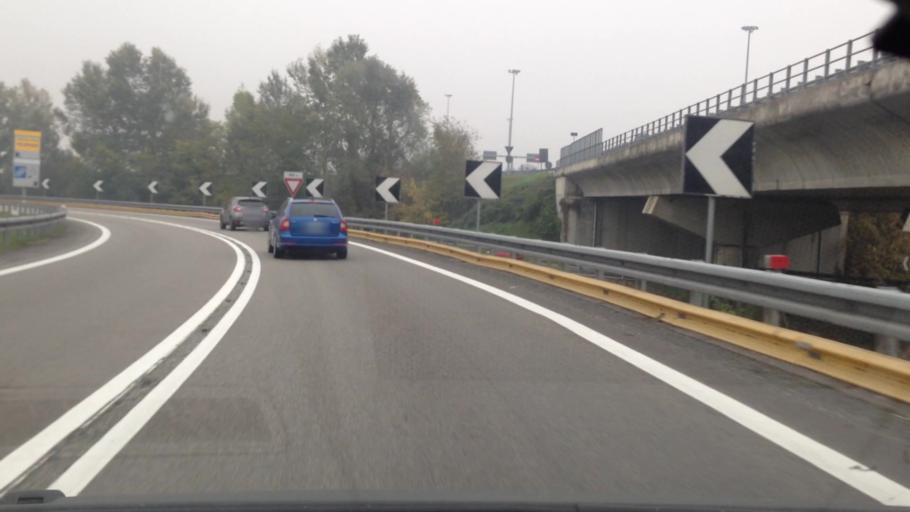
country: IT
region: Piedmont
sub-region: Provincia di Asti
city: Asti
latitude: 44.9090
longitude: 8.2449
